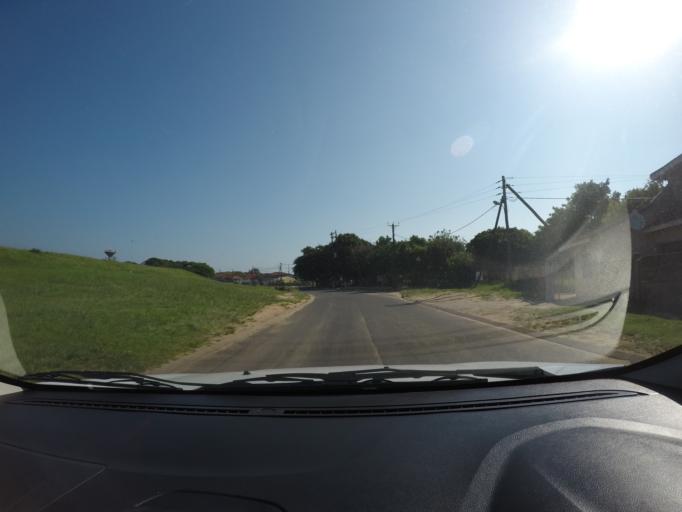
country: ZA
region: KwaZulu-Natal
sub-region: uThungulu District Municipality
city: Richards Bay
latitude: -28.7191
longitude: 32.0396
